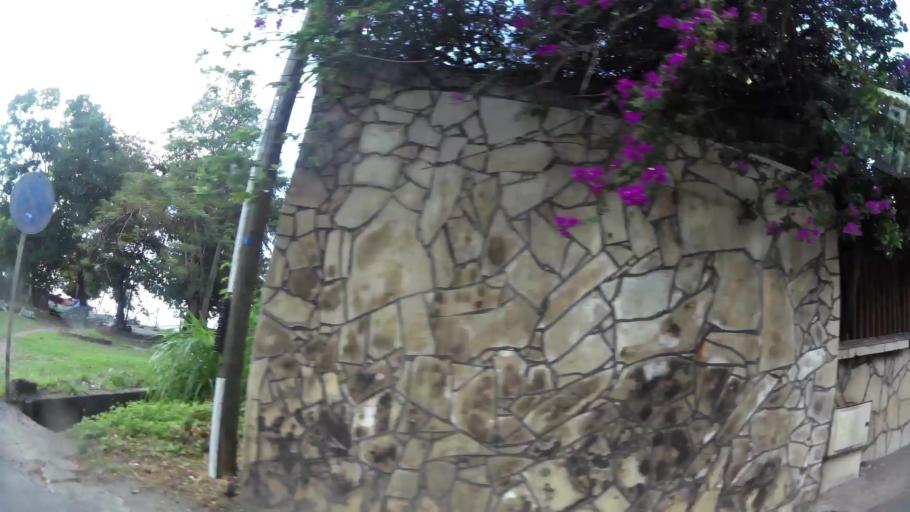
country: MQ
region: Martinique
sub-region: Martinique
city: Saint-Pierre
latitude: 14.7078
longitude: -61.1834
